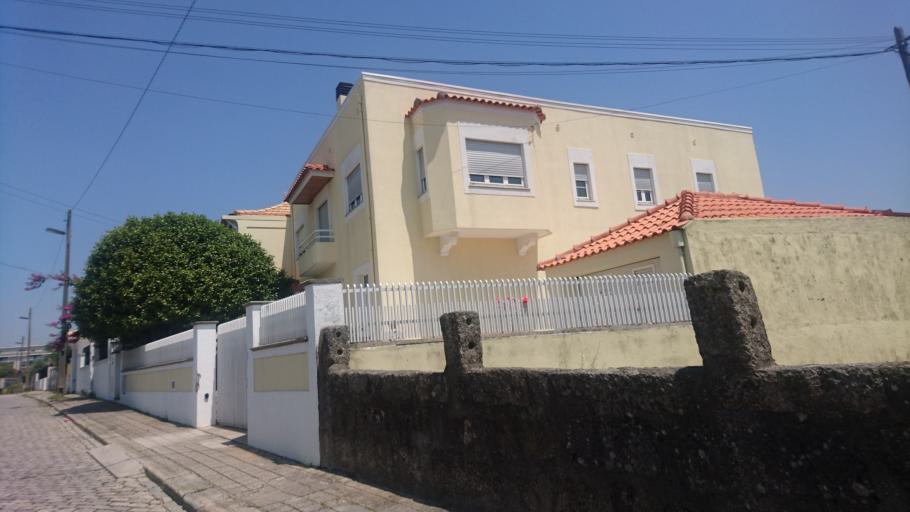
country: PT
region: Porto
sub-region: Gondomar
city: Rio Tinto
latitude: 41.1651
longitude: -8.5675
